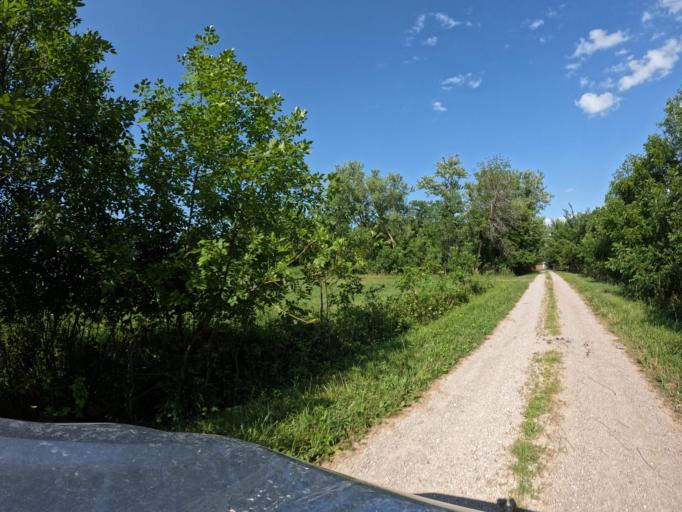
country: US
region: Iowa
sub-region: Appanoose County
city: Centerville
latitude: 40.7202
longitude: -93.0264
